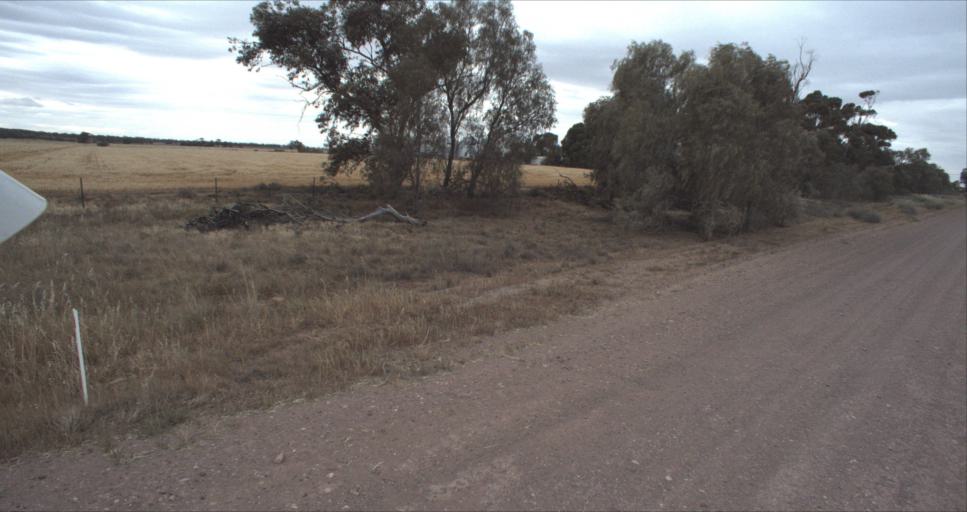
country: AU
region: New South Wales
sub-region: Leeton
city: Leeton
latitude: -34.4446
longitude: 146.3749
